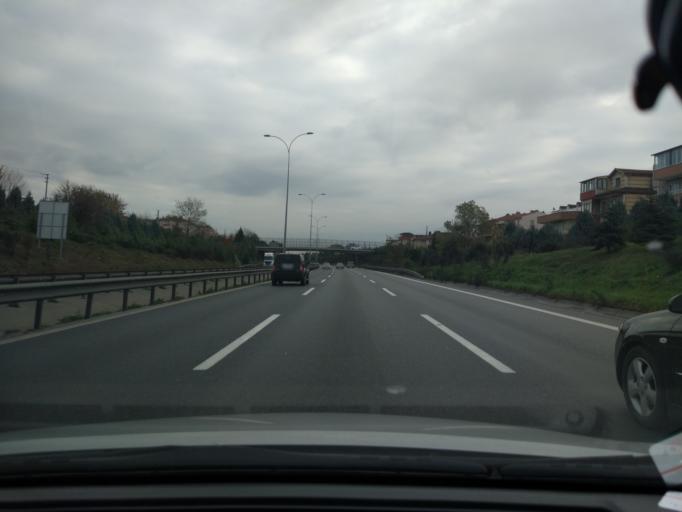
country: TR
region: Kocaeli
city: Derince
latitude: 40.7682
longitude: 29.8064
